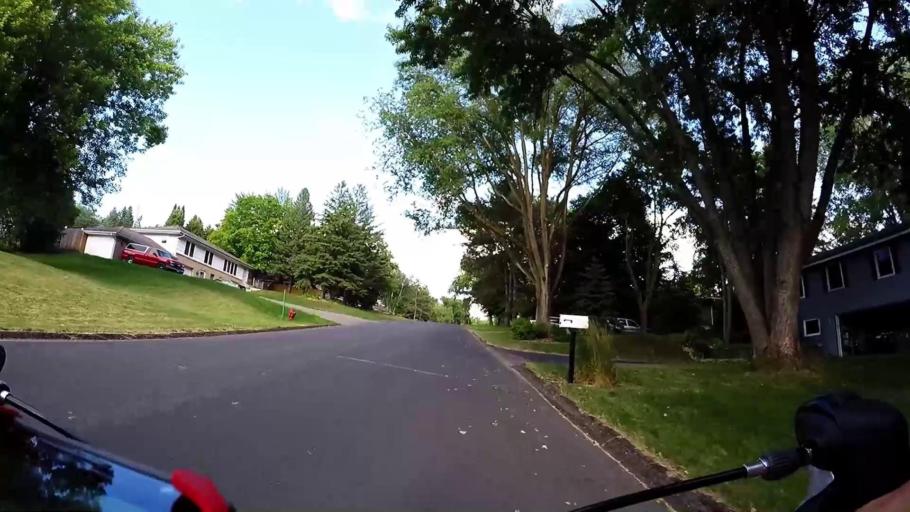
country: US
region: Minnesota
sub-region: Hennepin County
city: Eden Prairie
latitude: 44.8858
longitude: -93.4781
